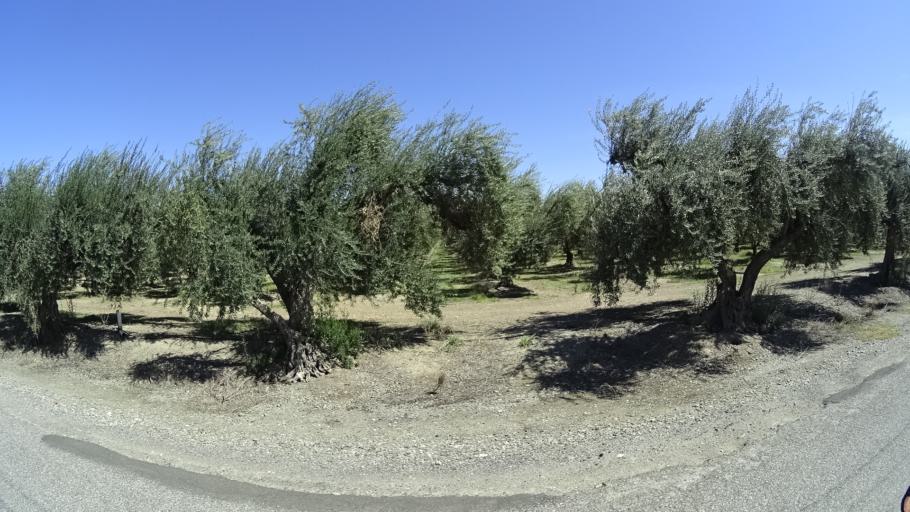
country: US
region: California
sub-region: Glenn County
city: Orland
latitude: 39.7485
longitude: -122.1504
